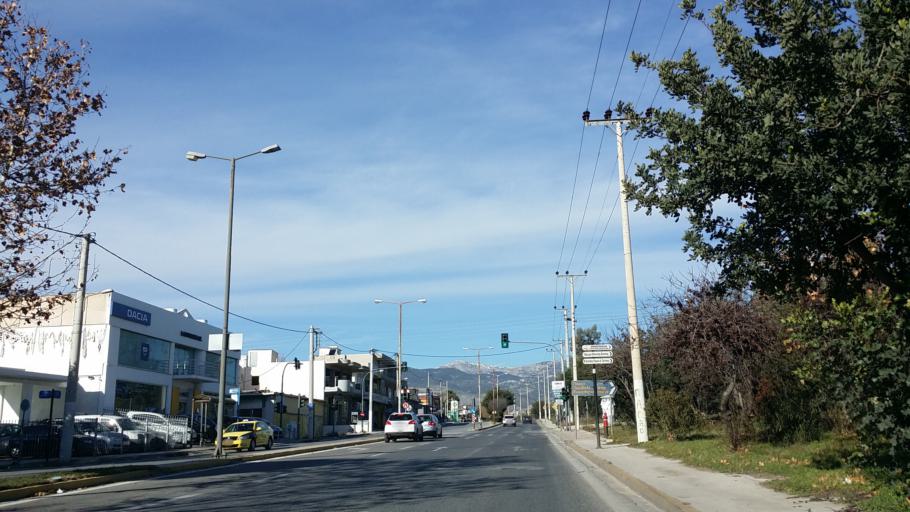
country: GR
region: Attica
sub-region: Nomarchia Athinas
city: Agioi Anargyroi
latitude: 38.0431
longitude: 23.7161
